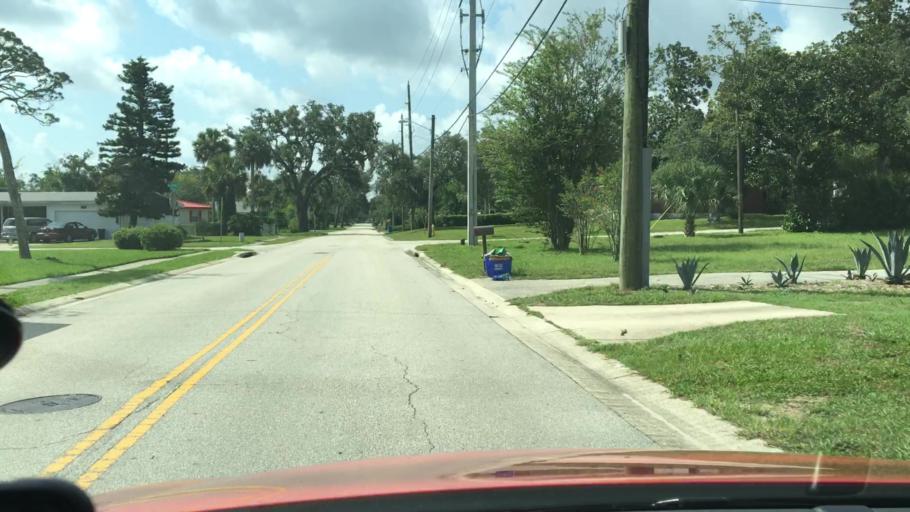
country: US
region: Florida
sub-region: Volusia County
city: Ormond Beach
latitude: 29.2736
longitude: -81.0534
